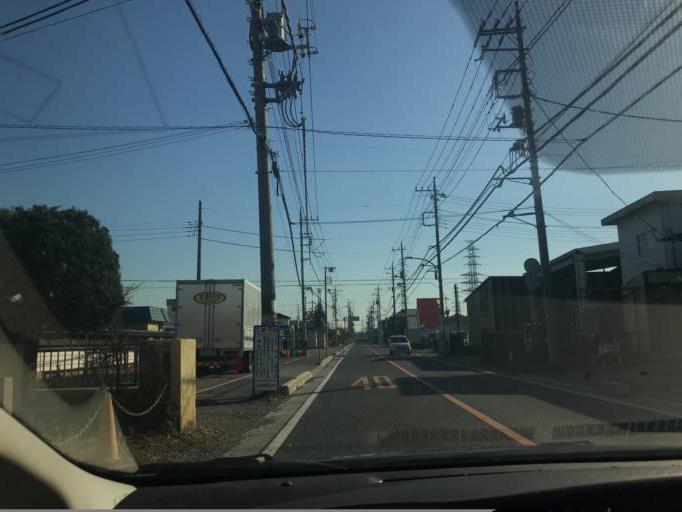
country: JP
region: Saitama
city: Yashio-shi
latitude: 35.8317
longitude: 139.8389
